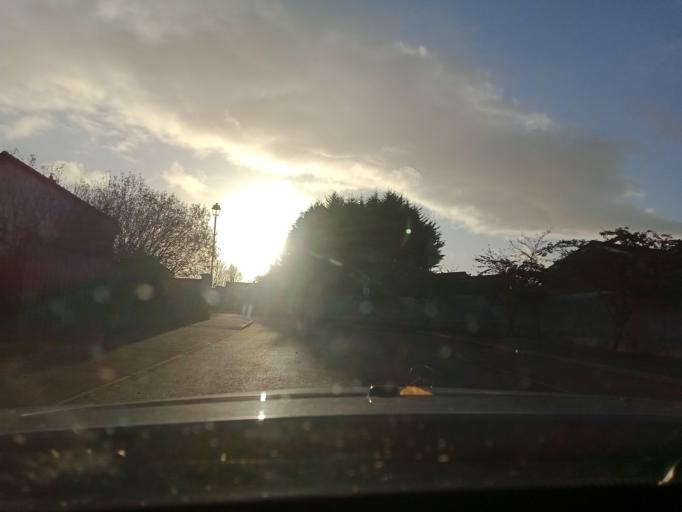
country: IE
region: Leinster
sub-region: Kilkenny
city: Callan
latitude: 52.5418
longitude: -7.3839
